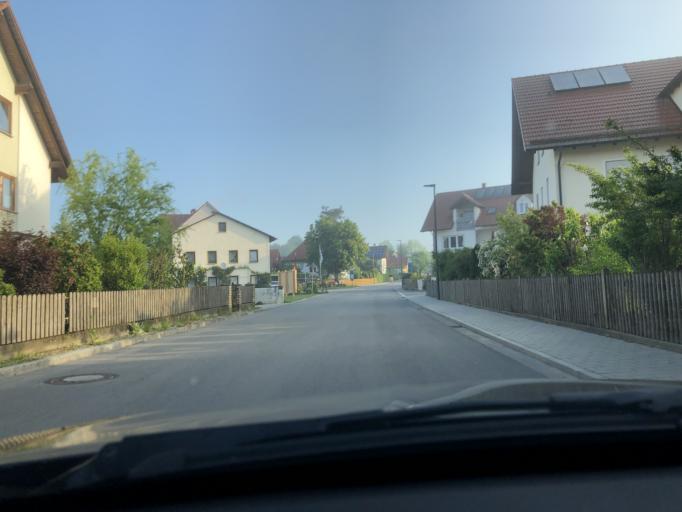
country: DE
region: Bavaria
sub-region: Upper Bavaria
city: Wolfersdorf
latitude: 48.4573
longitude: 11.7074
